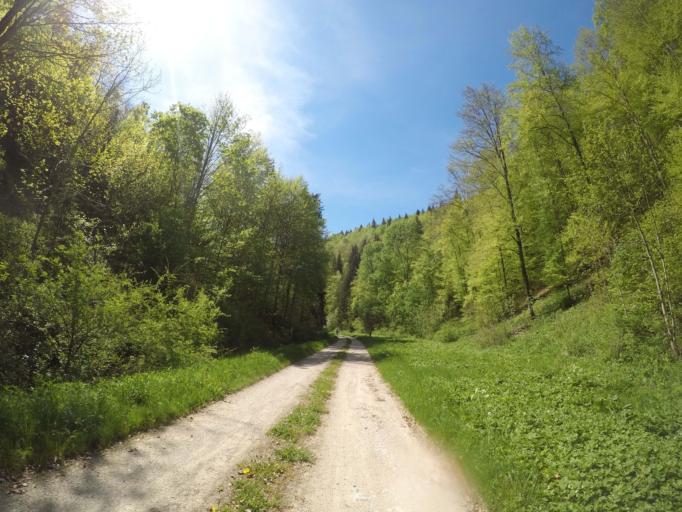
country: DE
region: Baden-Wuerttemberg
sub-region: Tuebingen Region
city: Schelklingen
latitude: 48.4138
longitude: 9.7188
